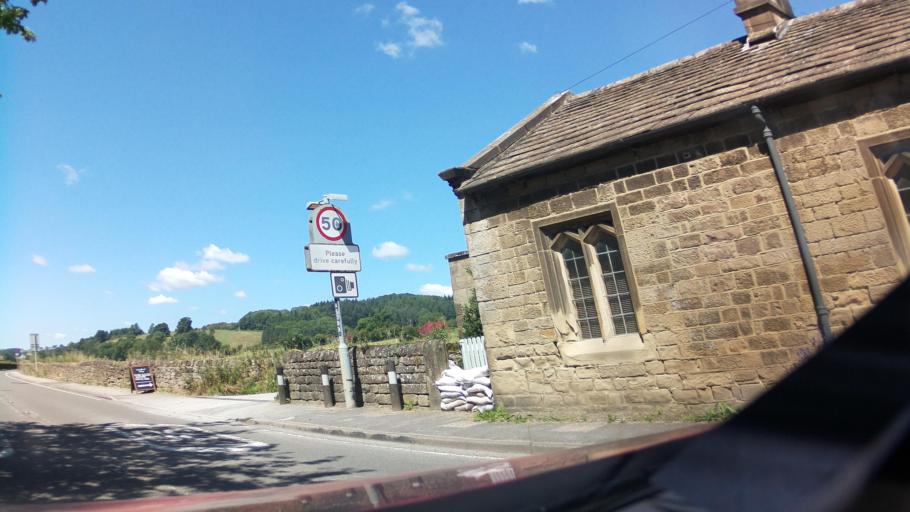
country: GB
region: England
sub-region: Derbyshire
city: Bakewell
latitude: 53.1887
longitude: -1.6197
